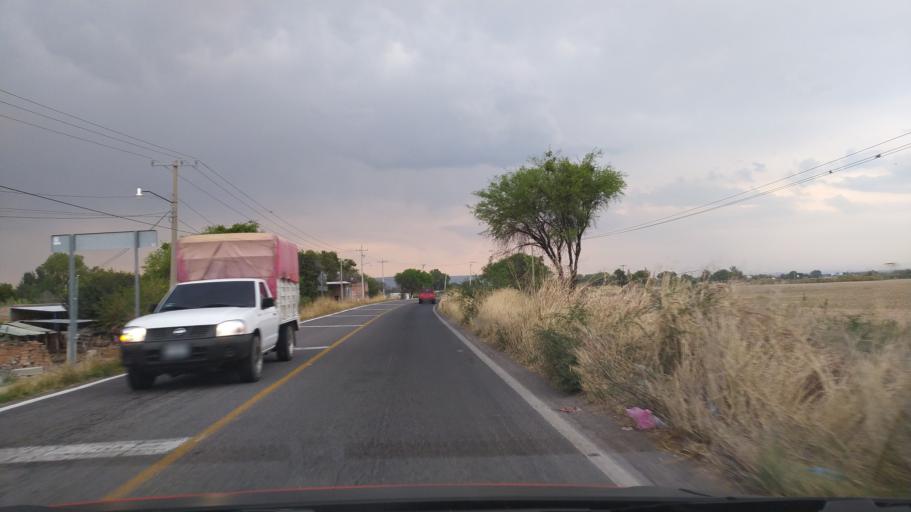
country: MX
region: Guanajuato
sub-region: San Francisco del Rincon
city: San Ignacio de Hidalgo
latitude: 20.8299
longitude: -101.9002
